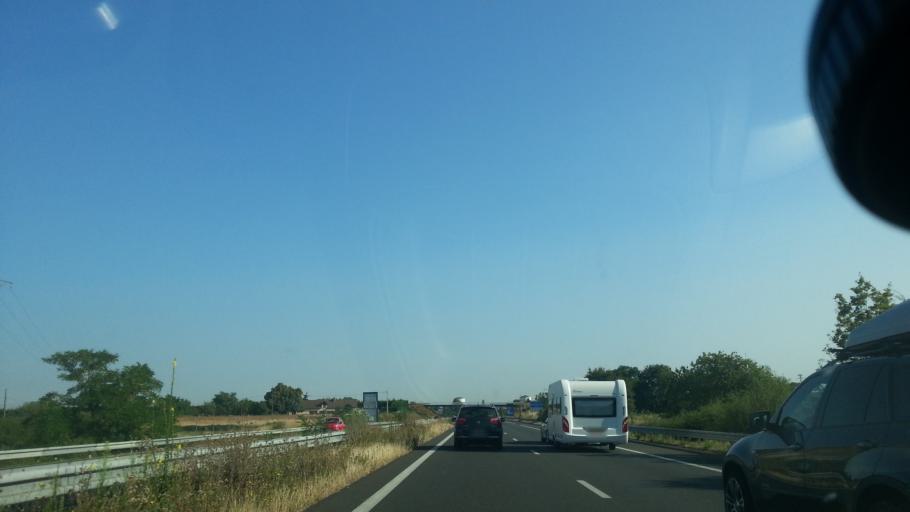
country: FR
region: Poitou-Charentes
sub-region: Departement de la Vienne
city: Chatellerault
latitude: 46.8102
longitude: 0.5139
